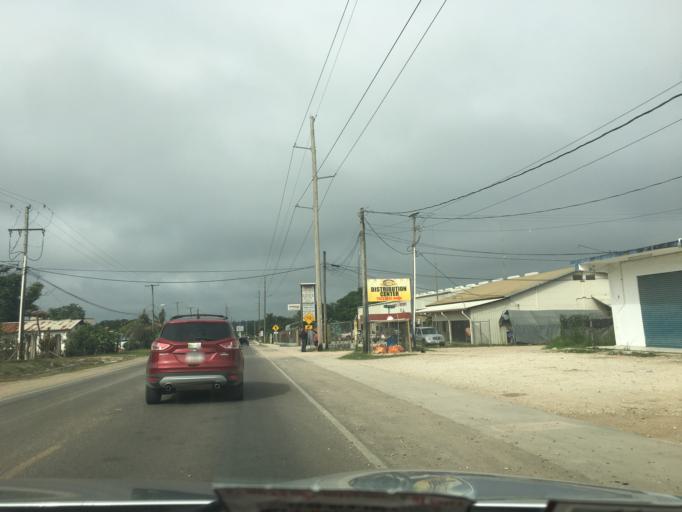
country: BZ
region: Cayo
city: Belmopan
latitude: 17.2500
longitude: -88.7822
